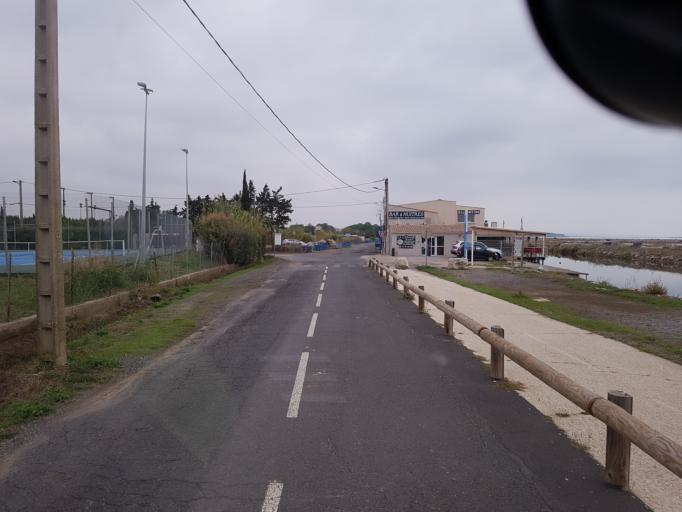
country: FR
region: Languedoc-Roussillon
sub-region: Departement de l'Herault
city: Marseillan
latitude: 43.3612
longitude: 3.5357
